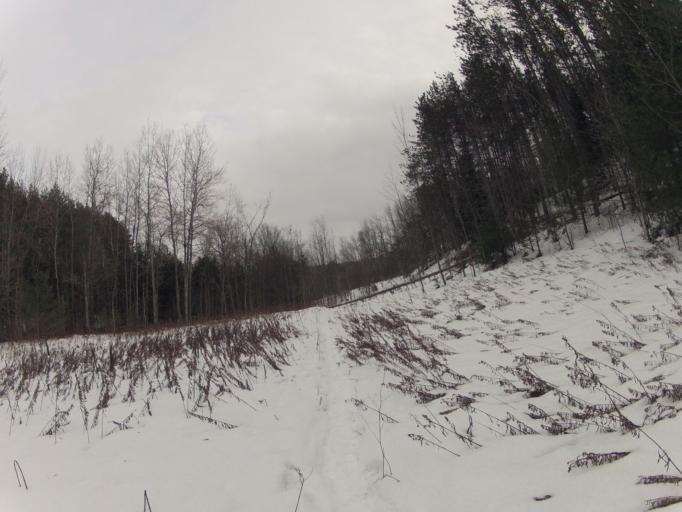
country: CA
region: Ontario
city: Orangeville
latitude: 43.9901
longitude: -80.0498
